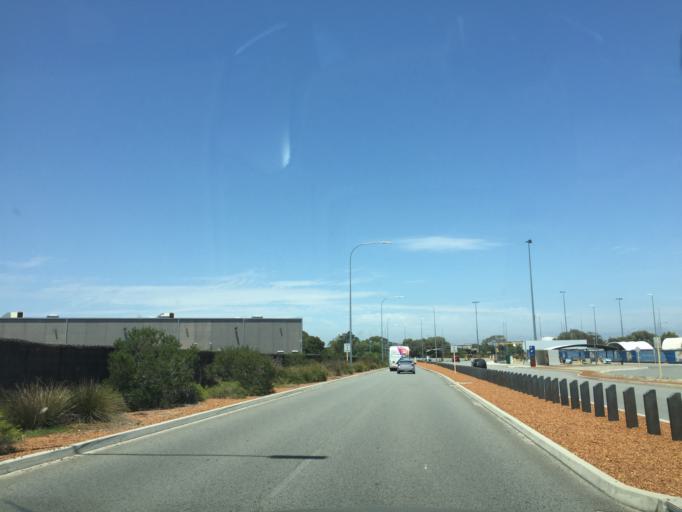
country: AU
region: Western Australia
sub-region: Belmont
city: Redcliffe
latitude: -31.9443
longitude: 115.9763
